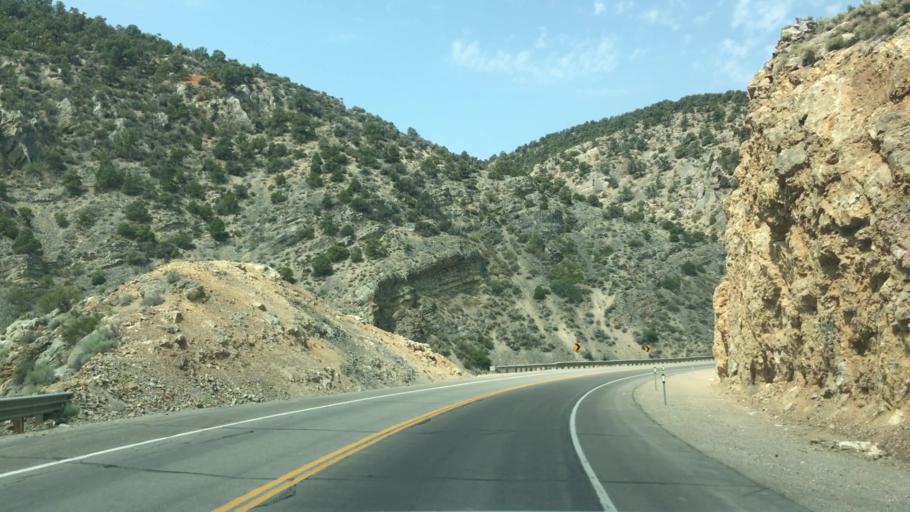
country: US
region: Nevada
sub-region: White Pine County
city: Ely
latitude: 39.2464
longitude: -114.9042
